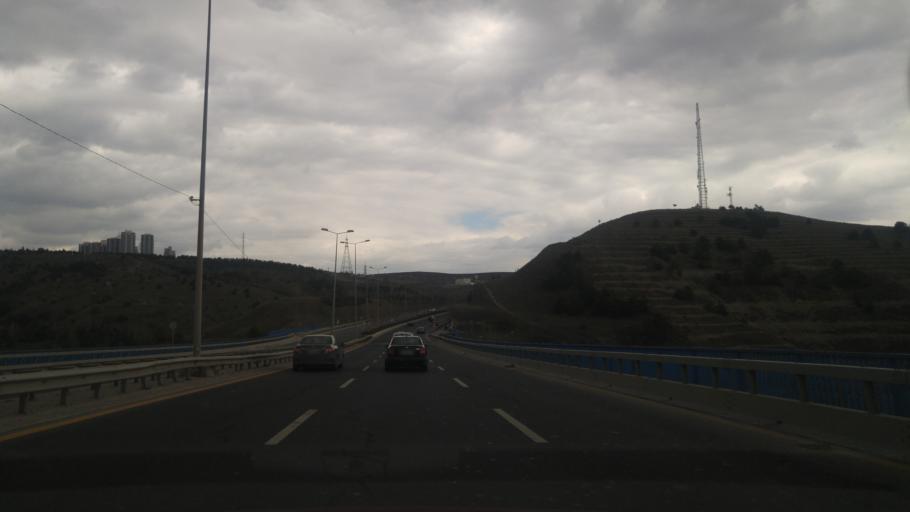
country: TR
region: Ankara
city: Mamak
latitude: 39.8887
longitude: 32.9095
